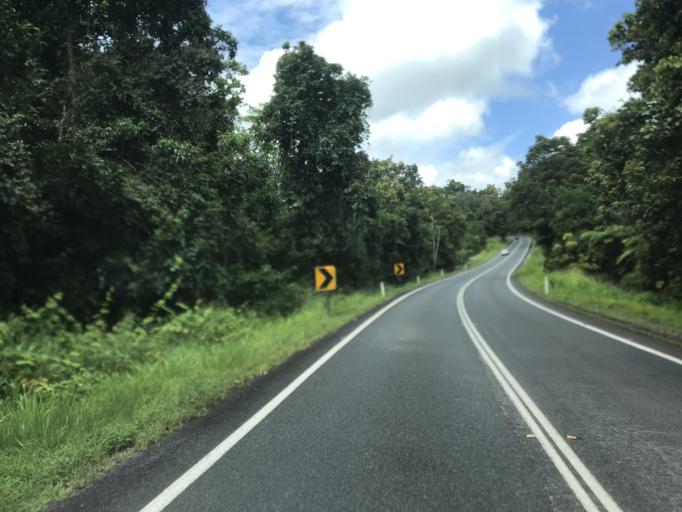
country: AU
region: Queensland
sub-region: Tablelands
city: Ravenshoe
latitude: -17.5932
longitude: 145.7345
